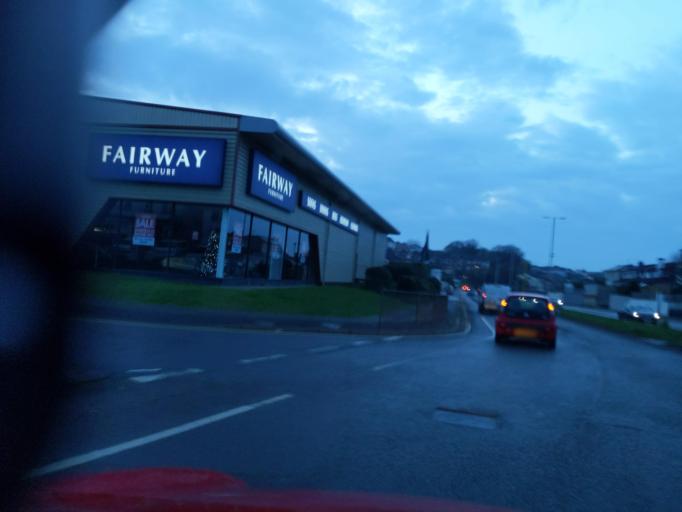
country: GB
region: England
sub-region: Plymouth
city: Plymstock
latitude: 50.3653
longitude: -4.0833
